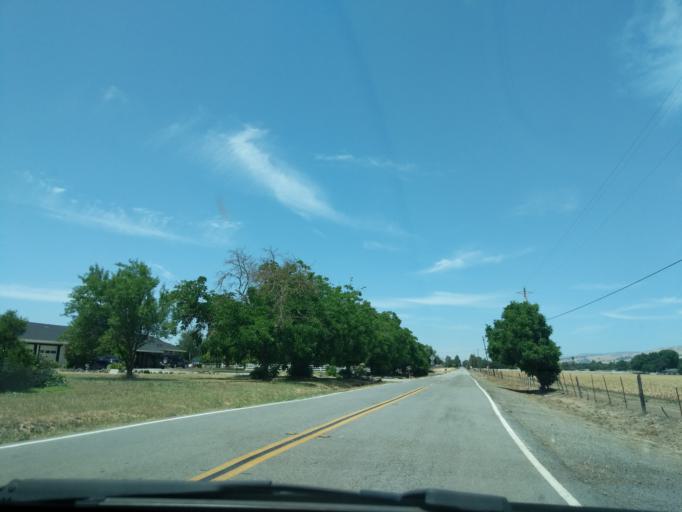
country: US
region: California
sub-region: Santa Clara County
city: Gilroy
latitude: 37.0511
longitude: -121.5637
